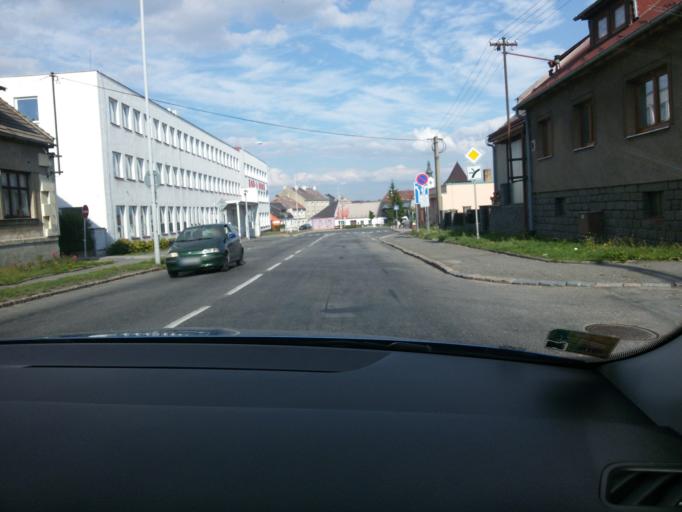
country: CZ
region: Pardubicky
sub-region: Okres Svitavy
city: Policka
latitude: 49.7146
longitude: 16.2596
